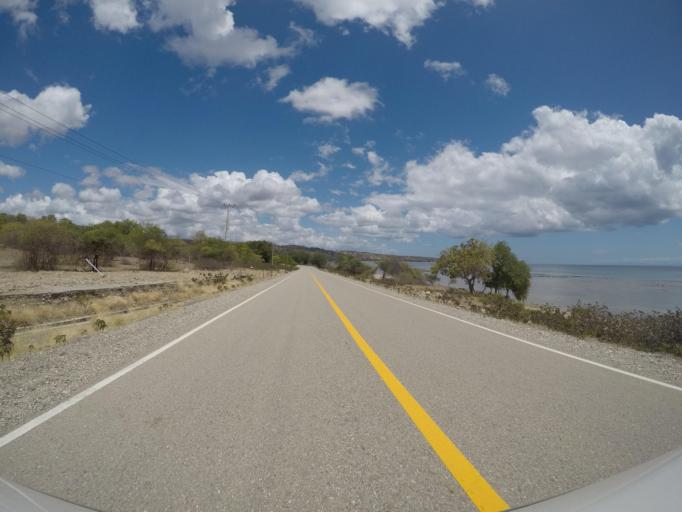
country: TL
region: Lautem
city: Lospalos
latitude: -8.4186
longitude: 126.7768
